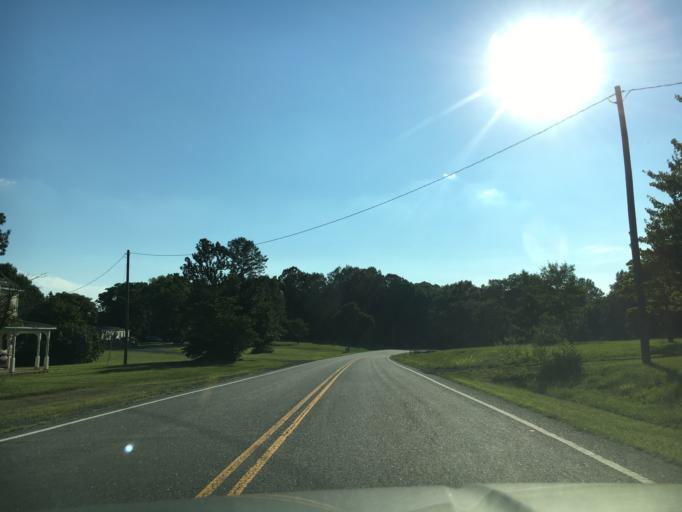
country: US
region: Virginia
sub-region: City of Bedford
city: Bedford
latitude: 37.2213
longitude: -79.4918
